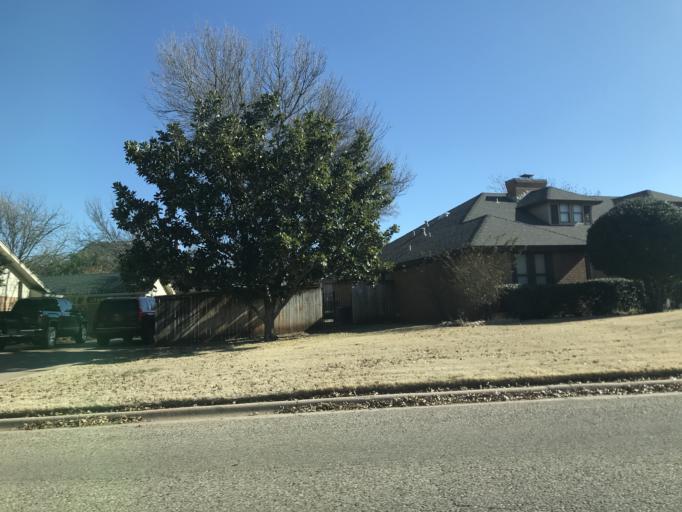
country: US
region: Texas
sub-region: Taylor County
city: Abilene
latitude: 32.3800
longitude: -99.7597
